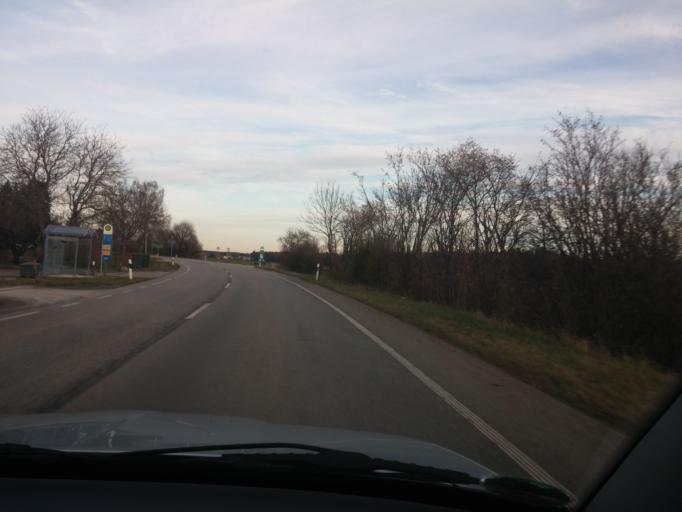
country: DE
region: Bavaria
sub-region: Upper Bavaria
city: Anzing
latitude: 48.1569
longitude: 11.8762
